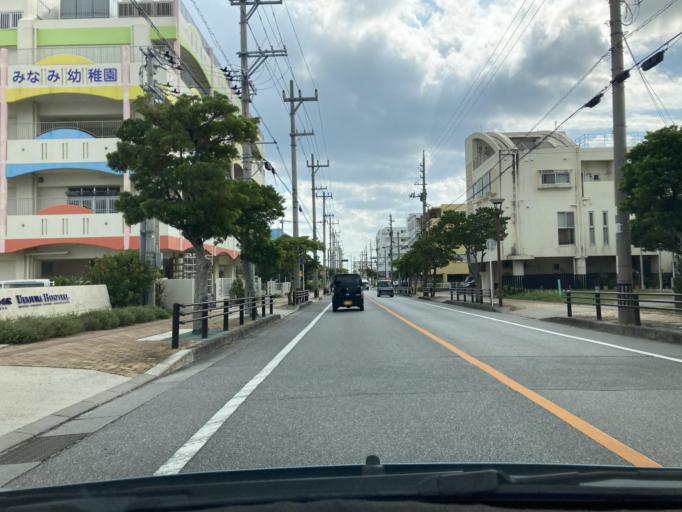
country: JP
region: Okinawa
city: Ginowan
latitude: 26.2491
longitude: 127.7735
